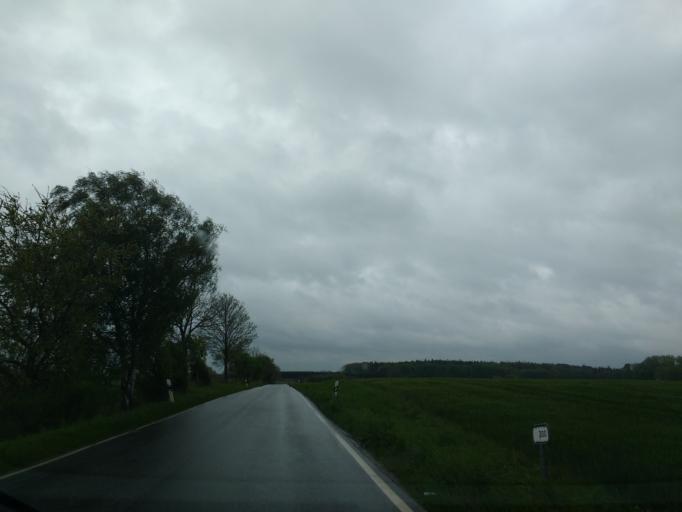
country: DE
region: Schleswig-Holstein
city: Loose
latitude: 54.5206
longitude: 9.9039
